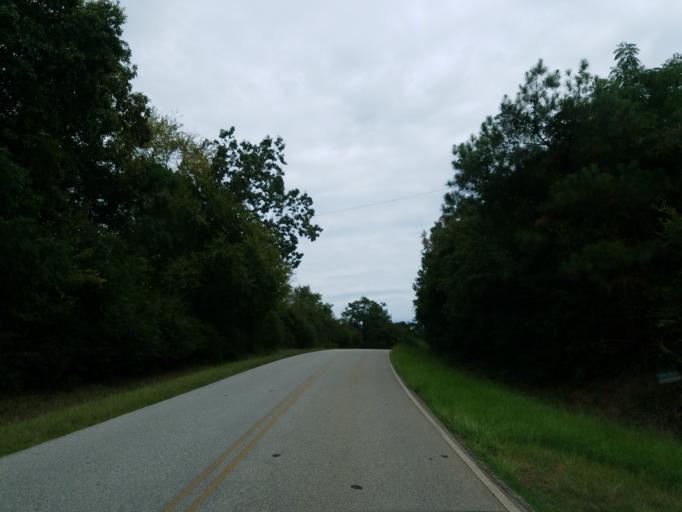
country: US
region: Georgia
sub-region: Bibb County
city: West Point
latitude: 32.8968
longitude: -83.8286
